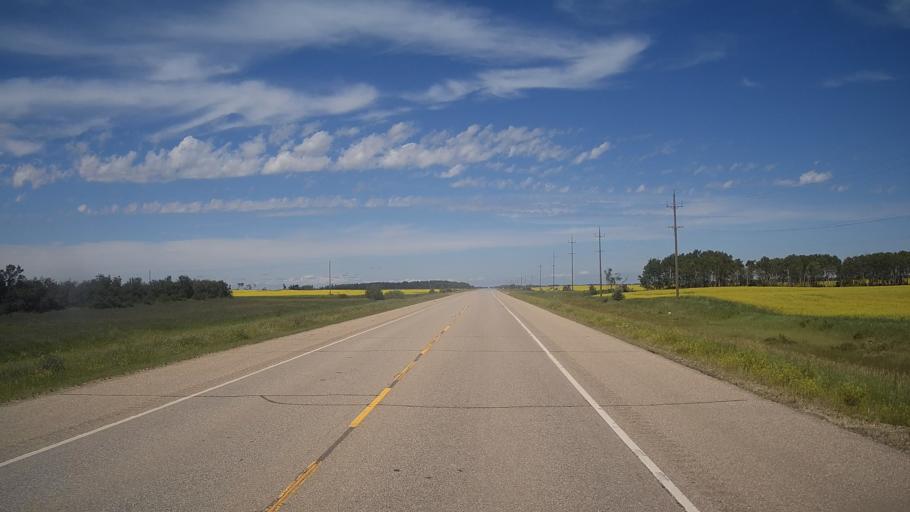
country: CA
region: Saskatchewan
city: Langenburg
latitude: 50.6657
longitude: -101.2761
